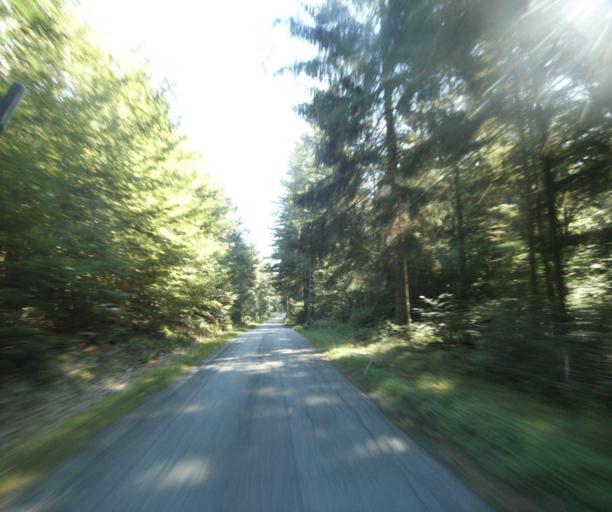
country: FR
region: Lorraine
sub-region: Departement des Vosges
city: Deyvillers
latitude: 48.1608
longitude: 6.5229
